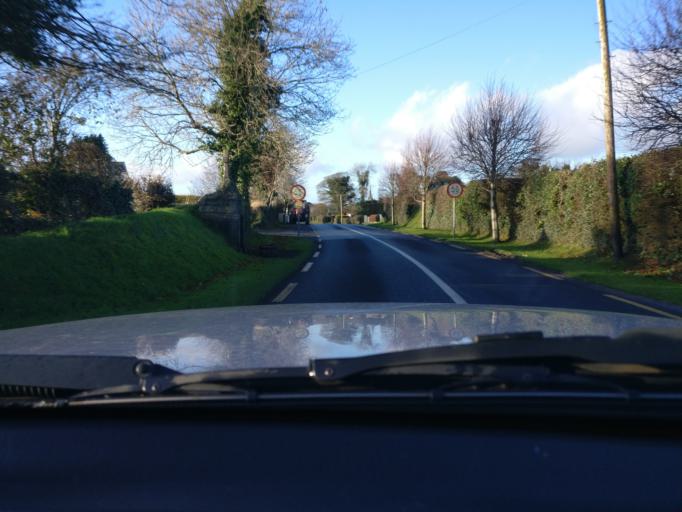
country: IE
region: Leinster
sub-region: An Mhi
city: Athboy
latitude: 53.6883
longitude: -6.9890
